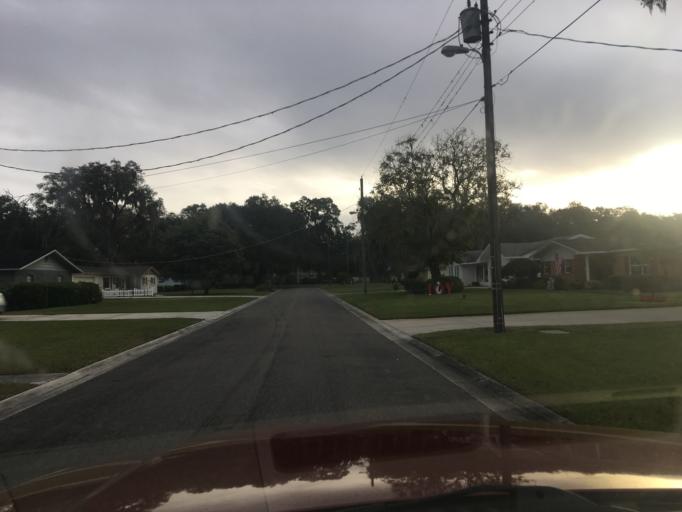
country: US
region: Florida
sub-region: Hillsborough County
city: Plant City
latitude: 28.0354
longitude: -82.0982
